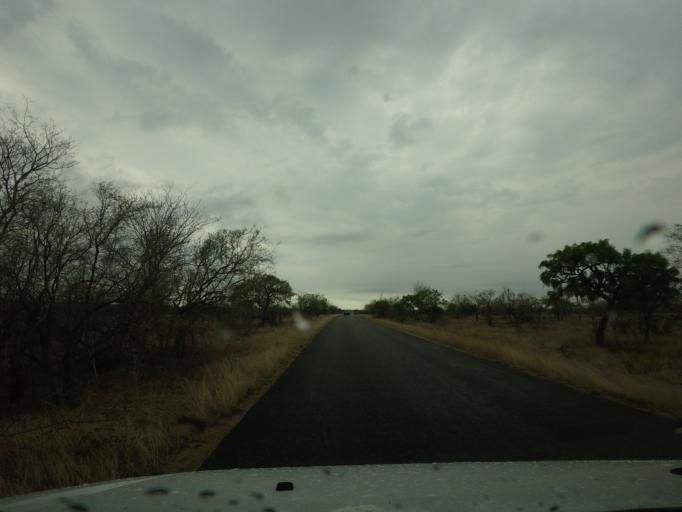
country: ZA
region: Limpopo
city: Thulamahashi
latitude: -24.4732
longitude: 31.4086
